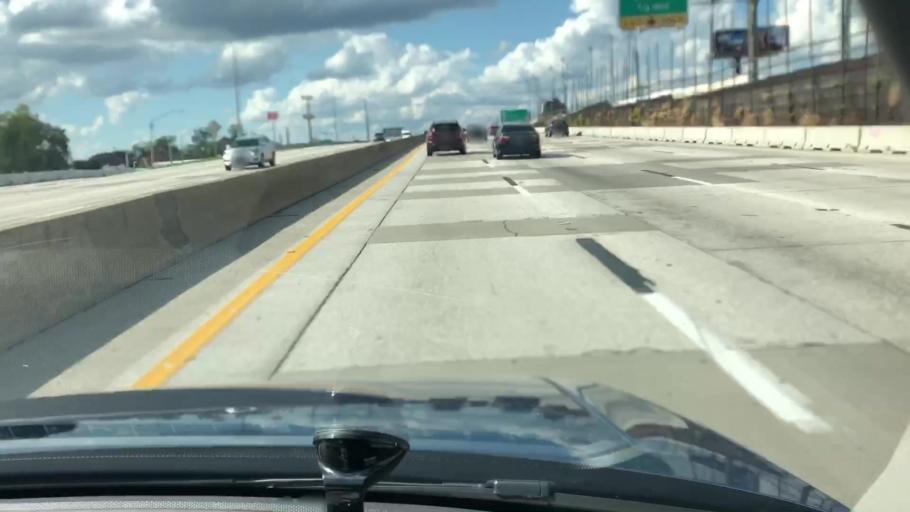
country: US
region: Florida
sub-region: Orange County
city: Fairview Shores
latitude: 28.5920
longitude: -81.3808
